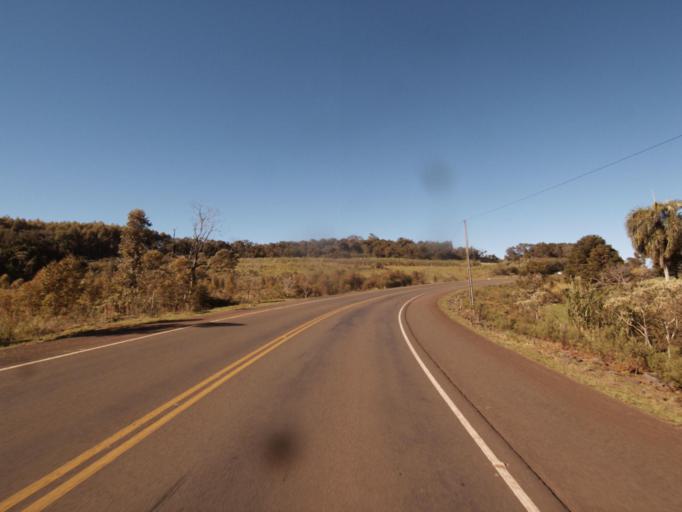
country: AR
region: Misiones
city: Bernardo de Irigoyen
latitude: -26.6695
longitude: -53.5901
